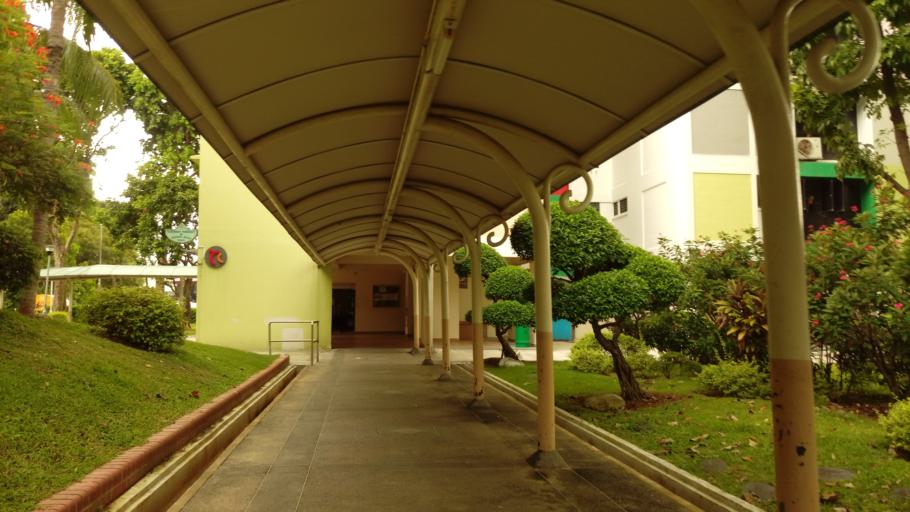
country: SG
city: Singapore
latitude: 1.2744
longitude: 103.8352
